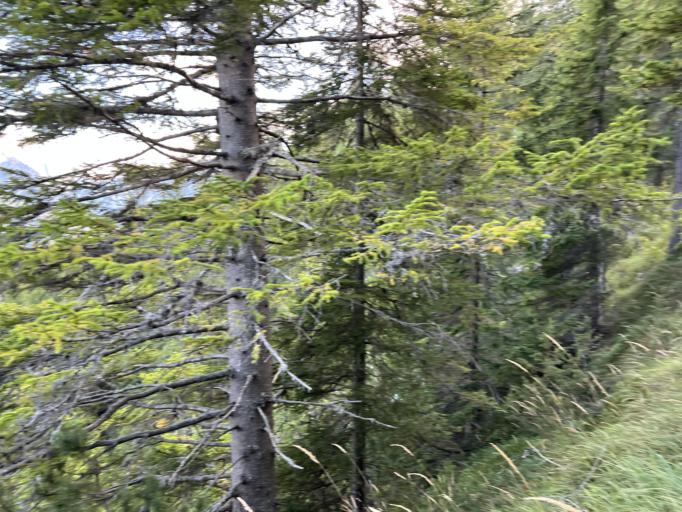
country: IT
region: Veneto
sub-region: Provincia di Belluno
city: San Pietro di Cadore
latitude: 46.6070
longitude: 12.5887
